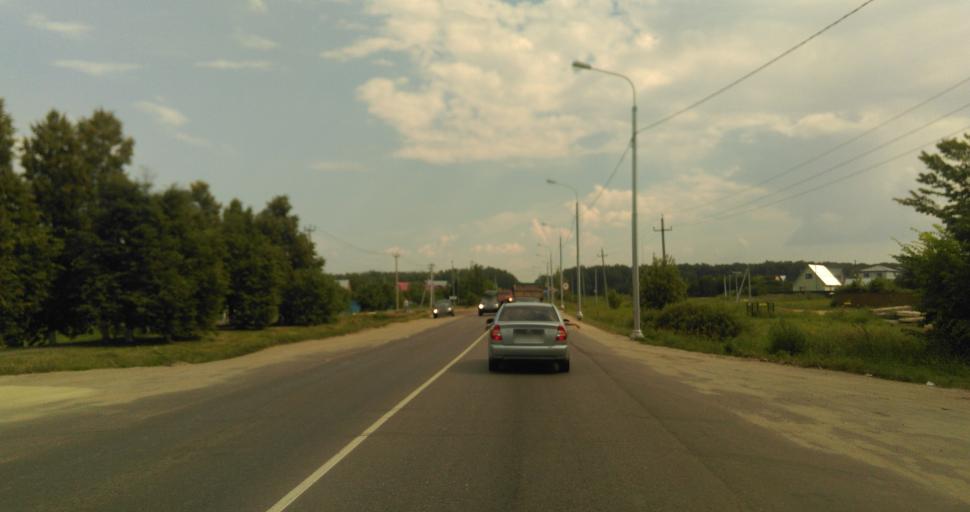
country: RU
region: Moskovskaya
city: Zhitnevo
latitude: 55.3411
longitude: 37.9065
